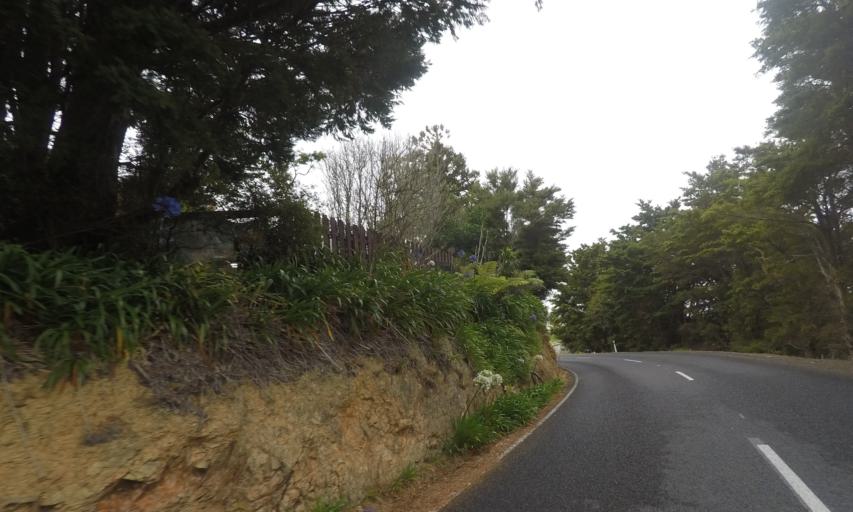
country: NZ
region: Northland
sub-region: Whangarei
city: Whangarei
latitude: -35.7595
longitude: 174.4551
